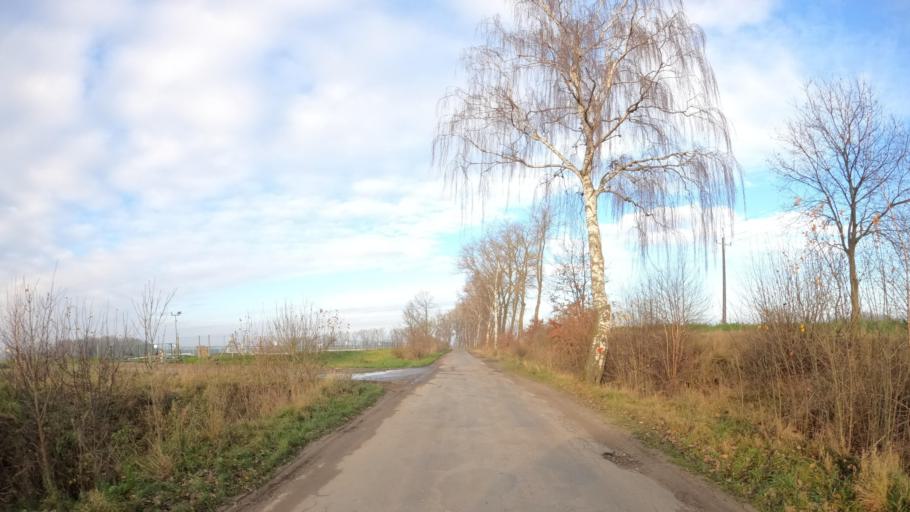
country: PL
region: West Pomeranian Voivodeship
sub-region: Powiat goleniowski
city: Maszewo
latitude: 53.5719
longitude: 15.0913
